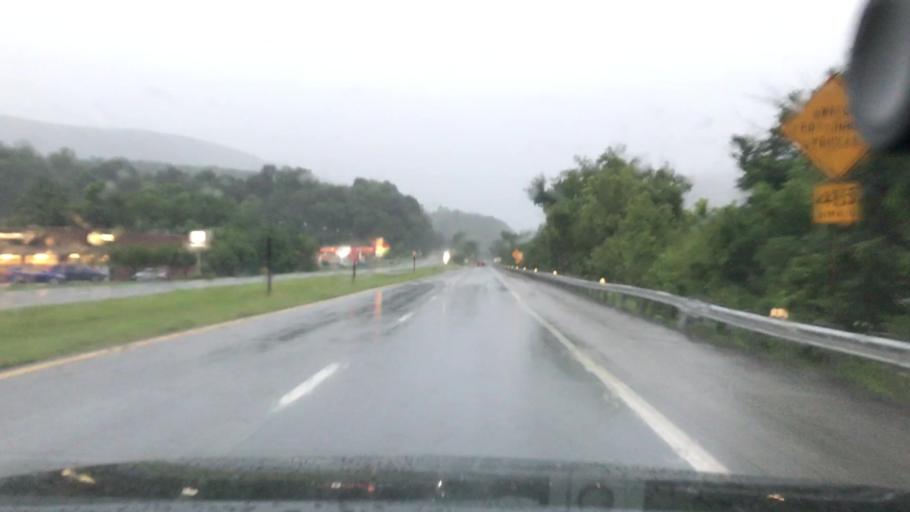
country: US
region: Virginia
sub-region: Giles County
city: Narrows
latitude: 37.3823
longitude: -80.8244
